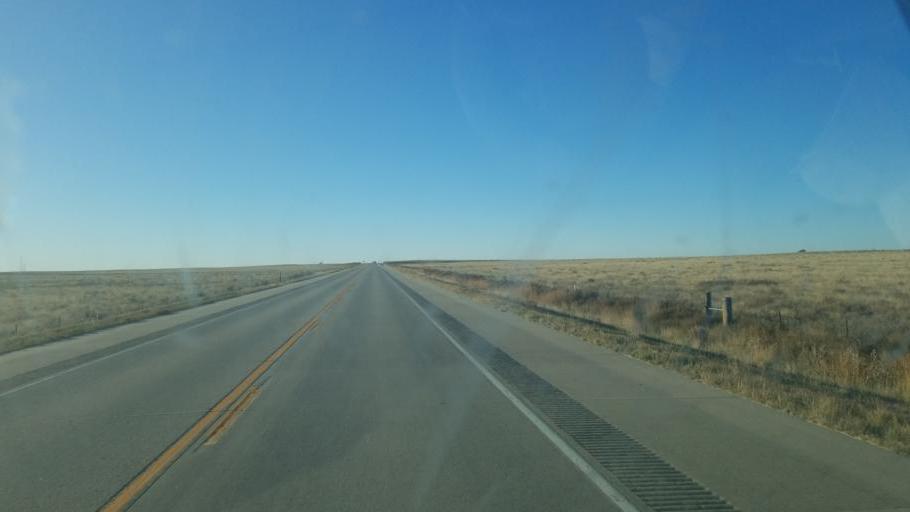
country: US
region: Colorado
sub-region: Kiowa County
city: Eads
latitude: 38.5351
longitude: -102.7858
